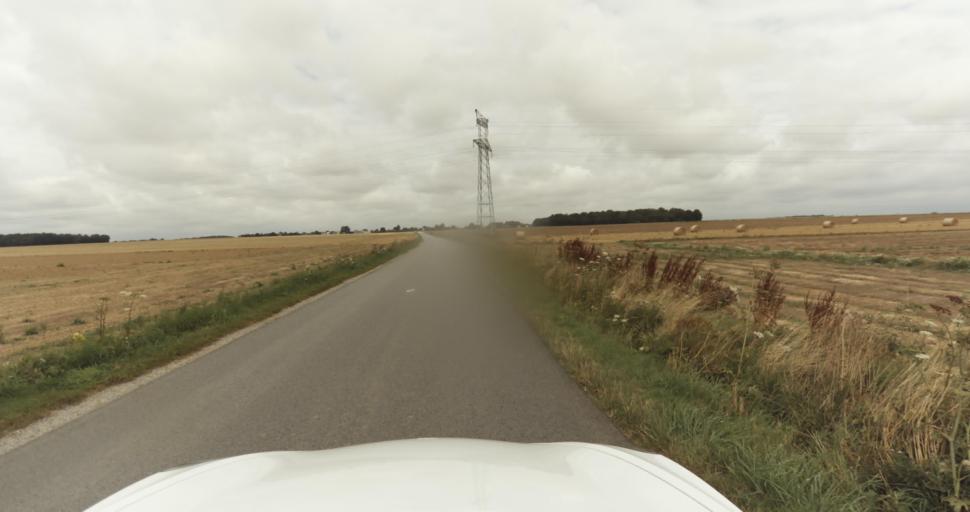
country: FR
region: Haute-Normandie
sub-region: Departement de l'Eure
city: Claville
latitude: 49.0349
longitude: 1.0286
